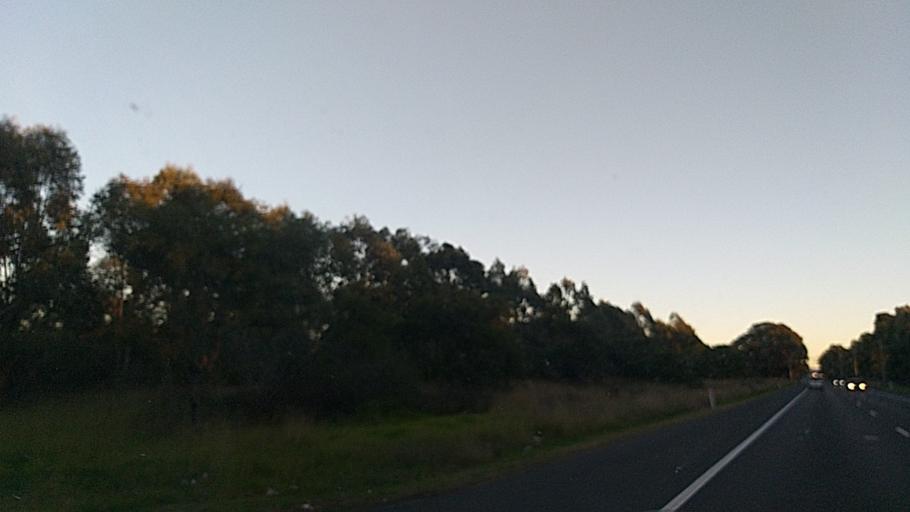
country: AU
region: New South Wales
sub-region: Hawkesbury
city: South Windsor
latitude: -33.6732
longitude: 150.8080
